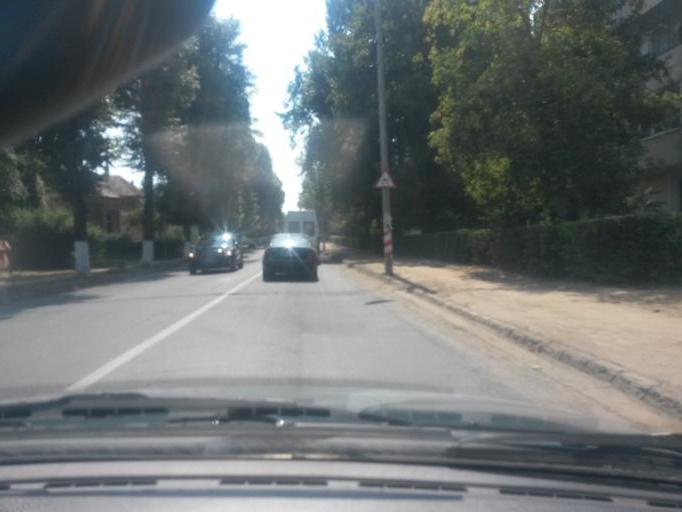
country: RO
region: Mures
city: Targu-Mures
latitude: 46.5504
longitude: 24.5735
